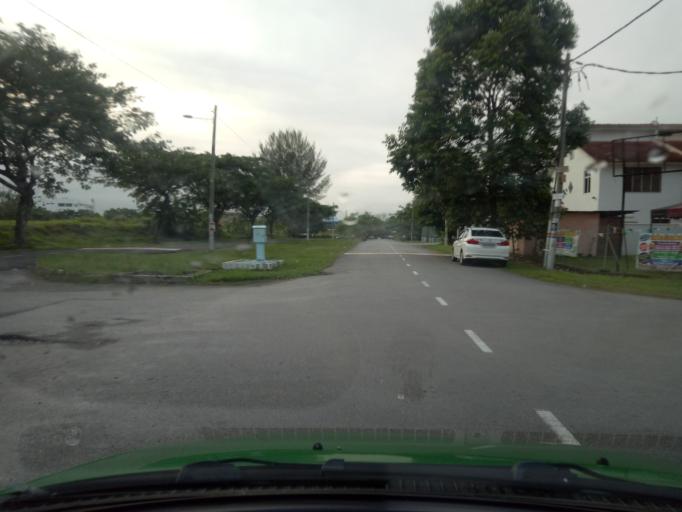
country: MY
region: Selangor
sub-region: Hulu Langat
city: Semenyih
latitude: 2.9307
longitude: 101.8640
